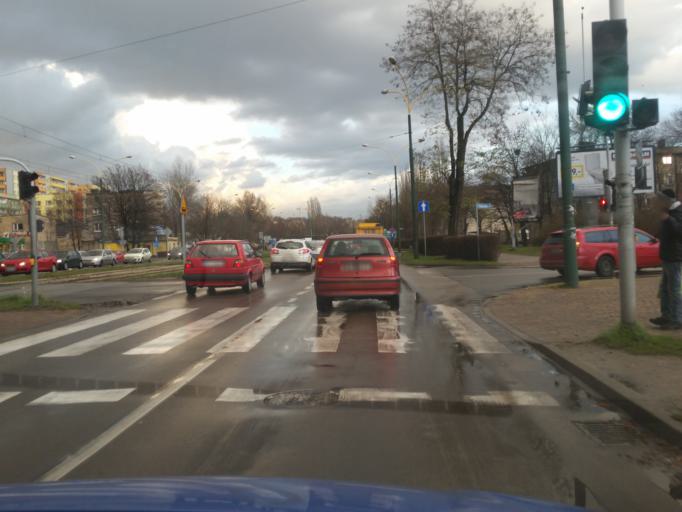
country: PL
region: Silesian Voivodeship
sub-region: Sosnowiec
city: Sosnowiec
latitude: 50.2734
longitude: 19.1412
